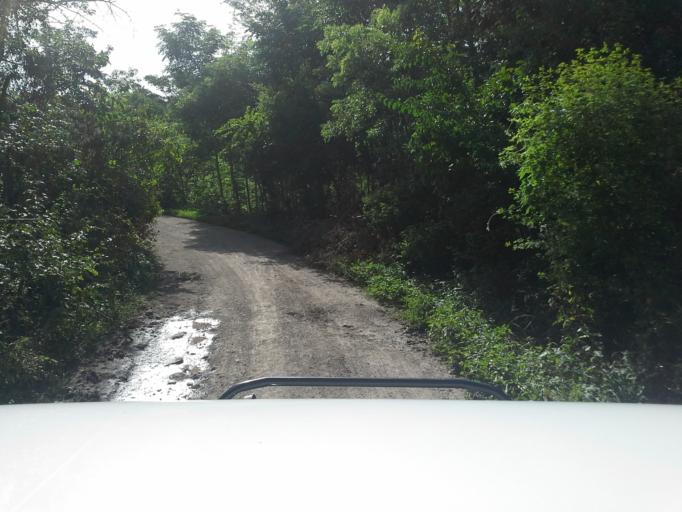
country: NI
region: Matagalpa
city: Ciudad Dario
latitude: 12.6720
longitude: -86.0524
